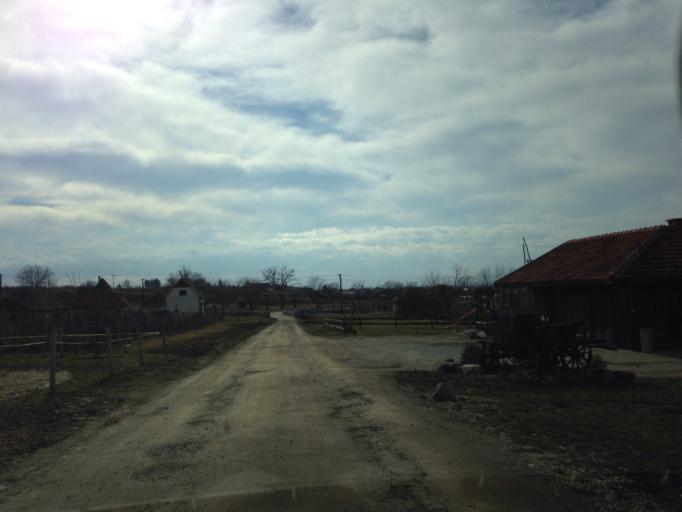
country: SK
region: Nitriansky
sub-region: Okres Komarno
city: Hurbanovo
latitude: 47.8470
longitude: 18.2767
